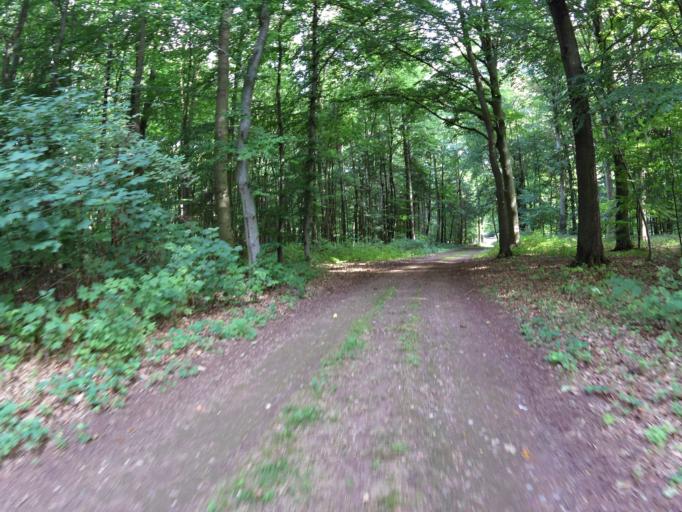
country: DE
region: Mecklenburg-Vorpommern
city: Seebad Bansin
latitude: 53.9472
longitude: 14.1001
